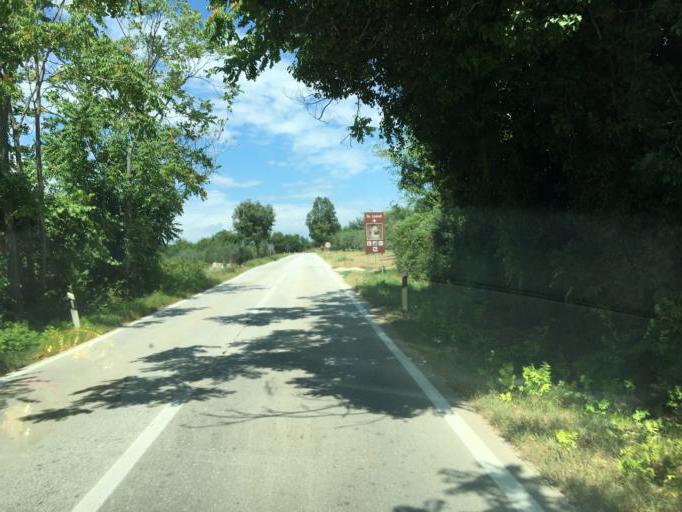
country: HR
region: Istarska
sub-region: Grad Rovinj
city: Rovinj
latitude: 45.1732
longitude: 13.7418
